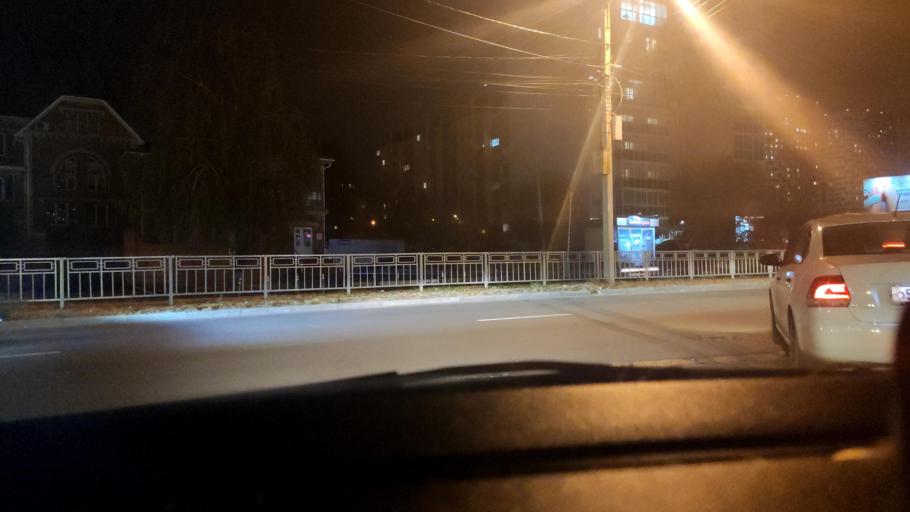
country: RU
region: Voronezj
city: Voronezh
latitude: 51.7112
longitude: 39.1953
